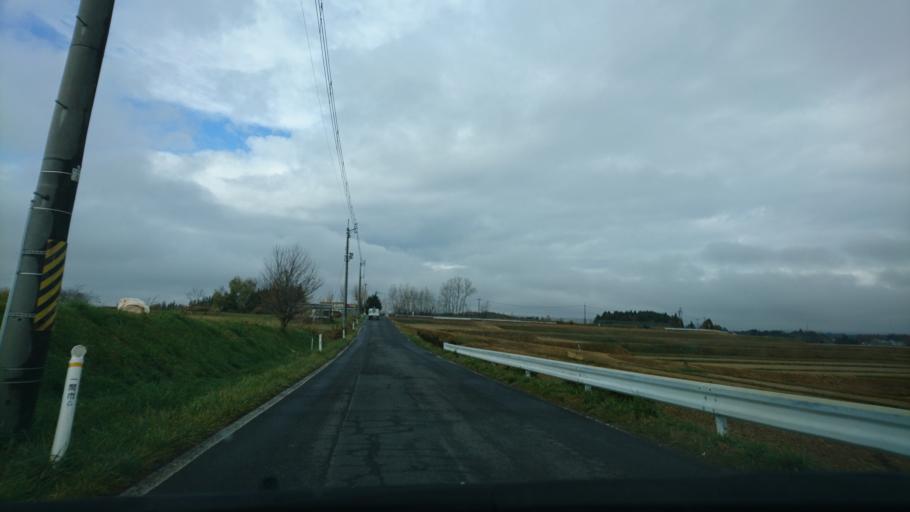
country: JP
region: Iwate
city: Ichinoseki
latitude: 38.8867
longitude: 141.1937
